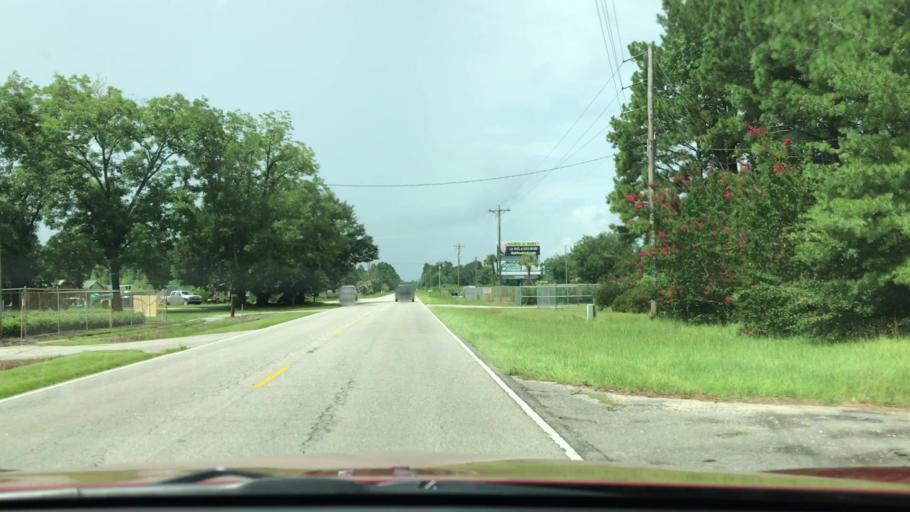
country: US
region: South Carolina
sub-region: Horry County
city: Red Hill
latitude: 33.8969
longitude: -78.9338
